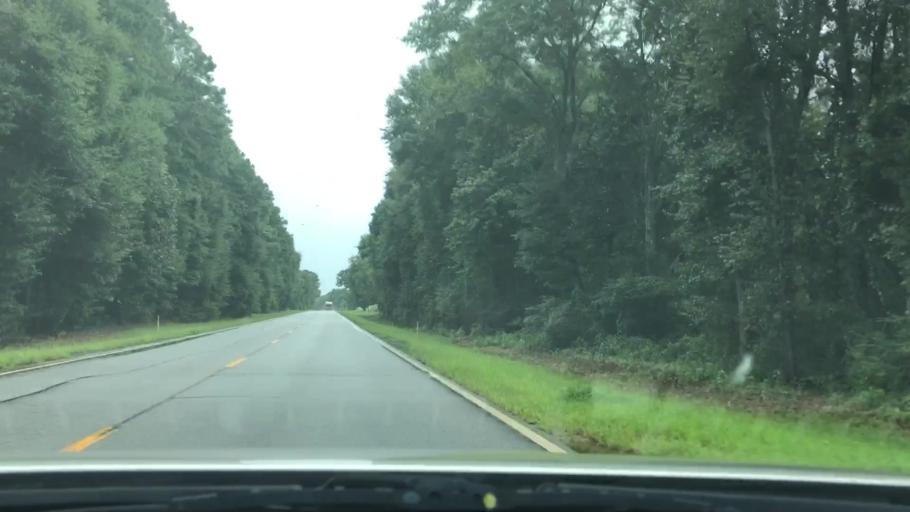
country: US
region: Georgia
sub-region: Pike County
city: Zebulon
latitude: 33.0893
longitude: -84.2745
